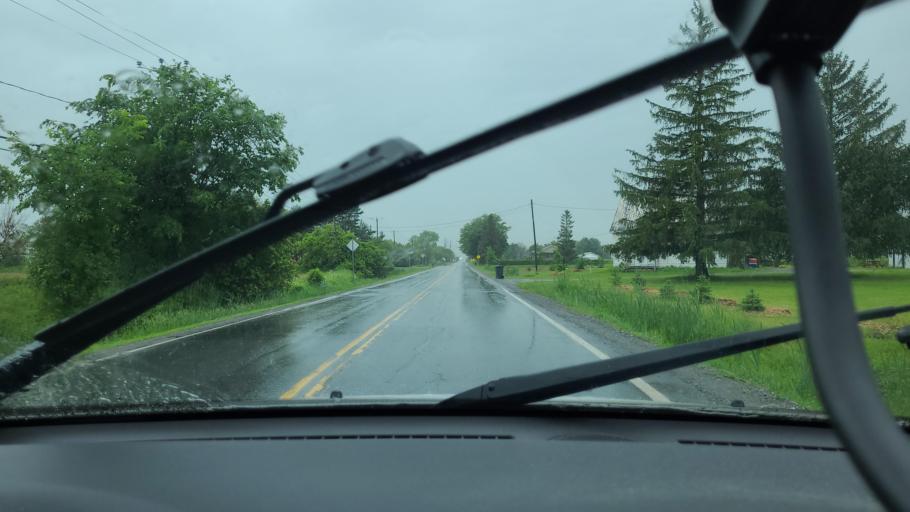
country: CA
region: Quebec
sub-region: Monteregie
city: Saint-Hyacinthe
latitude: 45.6176
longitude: -72.9899
